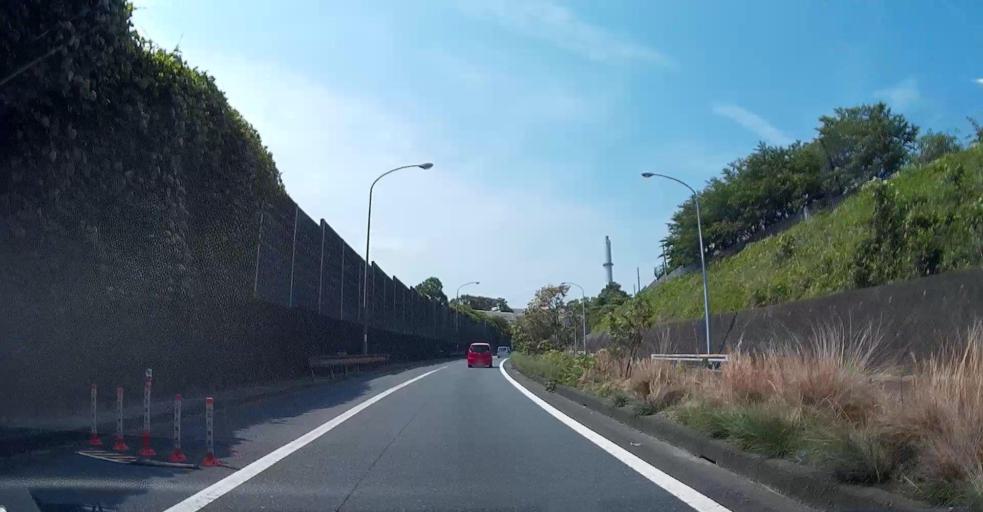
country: JP
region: Kanagawa
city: Yokohama
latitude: 35.4444
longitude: 139.5838
